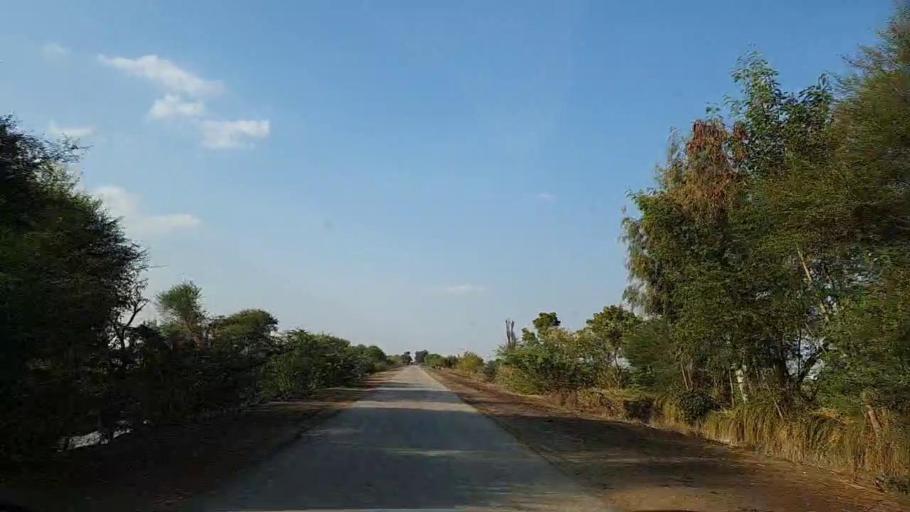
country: PK
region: Sindh
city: Tando Mittha Khan
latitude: 25.7284
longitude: 69.2134
